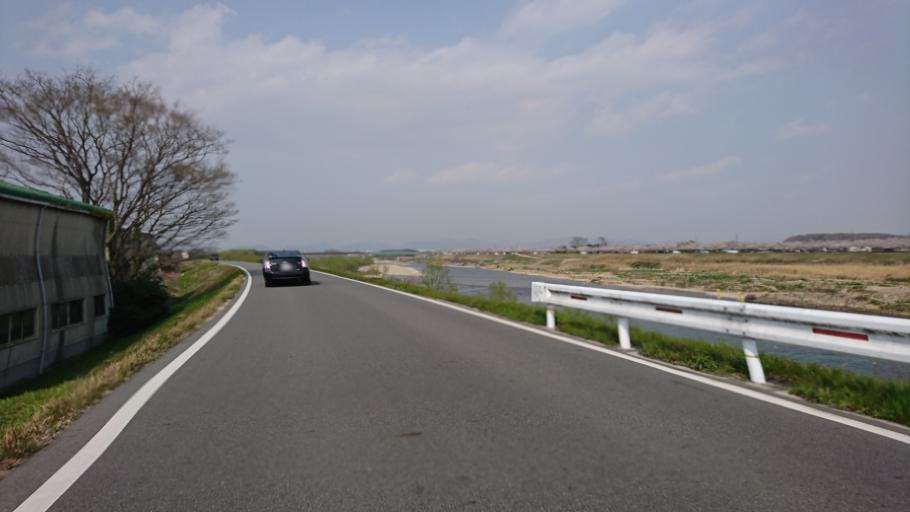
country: JP
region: Hyogo
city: Ono
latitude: 34.8707
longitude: 134.9226
